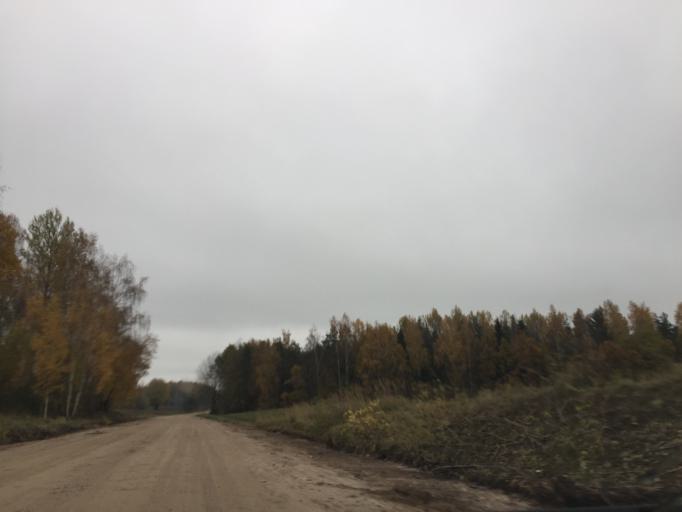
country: LV
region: Sigulda
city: Sigulda
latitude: 57.2742
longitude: 24.8416
